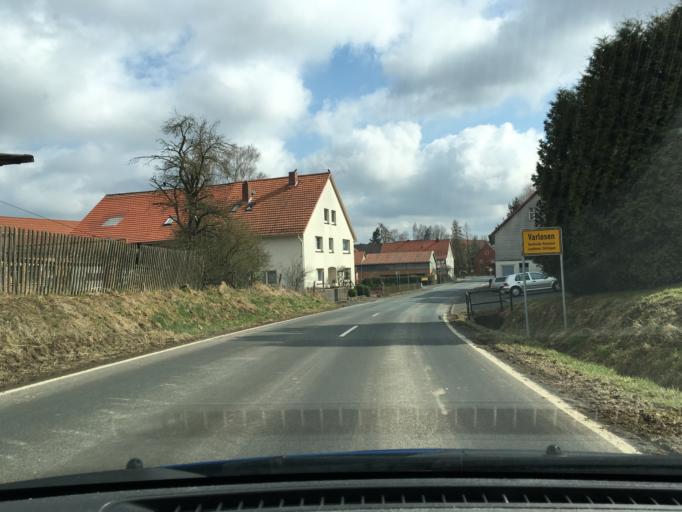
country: DE
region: Lower Saxony
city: Buhren
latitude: 51.5036
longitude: 9.7088
